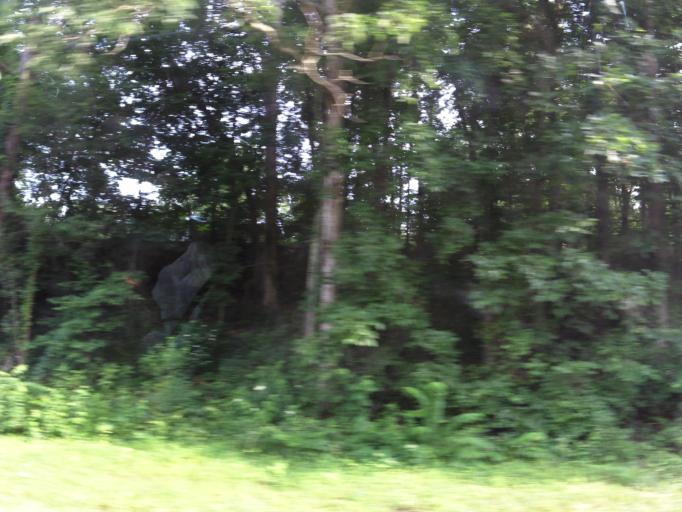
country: US
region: Tennessee
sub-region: Humphreys County
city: McEwen
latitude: 36.1027
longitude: -87.6667
